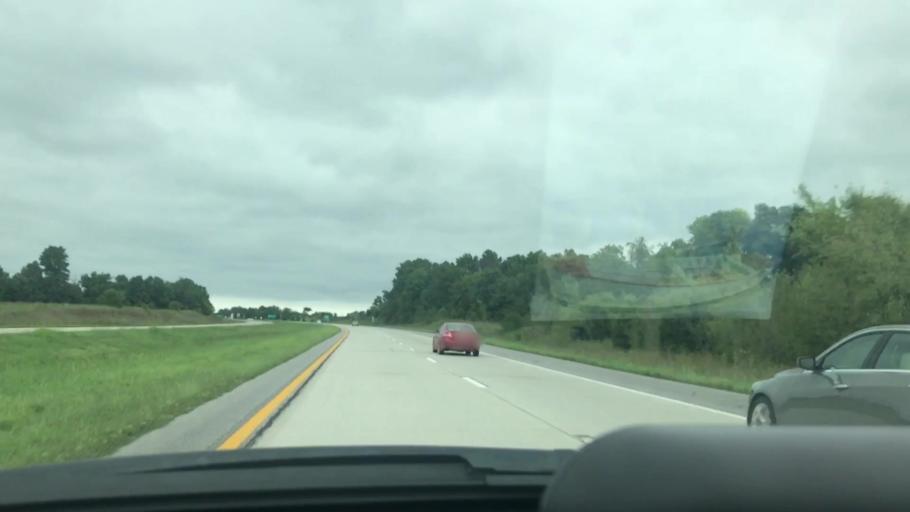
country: US
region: Missouri
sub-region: Greene County
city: Fair Grove
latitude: 37.4517
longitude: -93.1412
